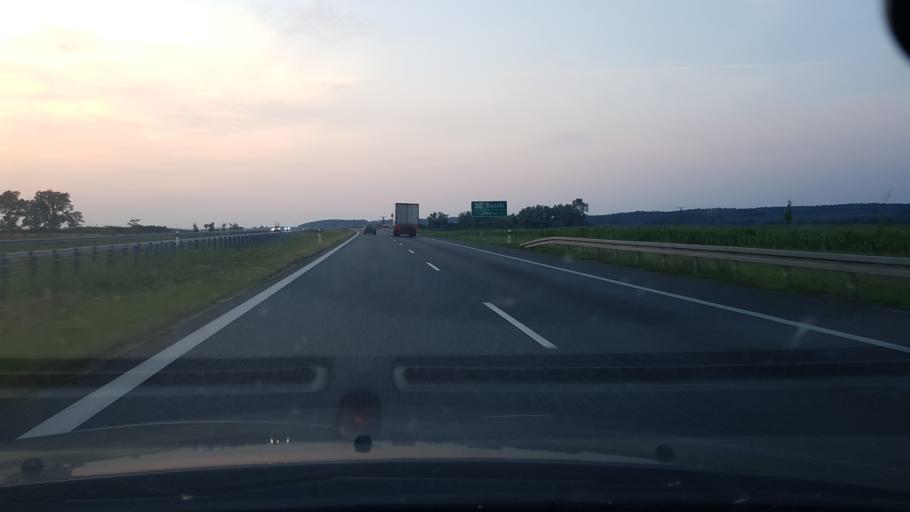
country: PL
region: Warmian-Masurian Voivodeship
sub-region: Powiat nidzicki
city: Nidzica
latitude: 53.3927
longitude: 20.3663
